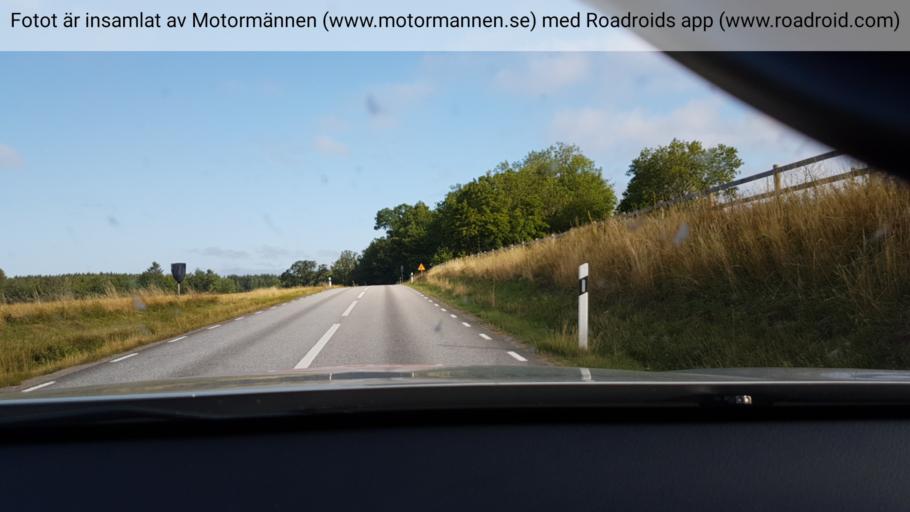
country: SE
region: Stockholm
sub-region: Norrtalje Kommun
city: Rimbo
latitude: 59.6912
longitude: 18.3709
